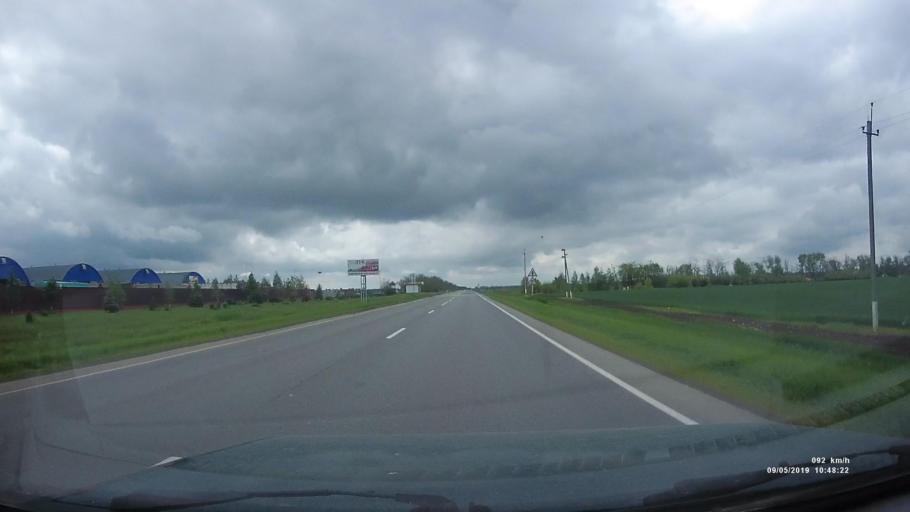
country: RU
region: Rostov
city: Peshkovo
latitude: 46.9574
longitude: 39.3558
